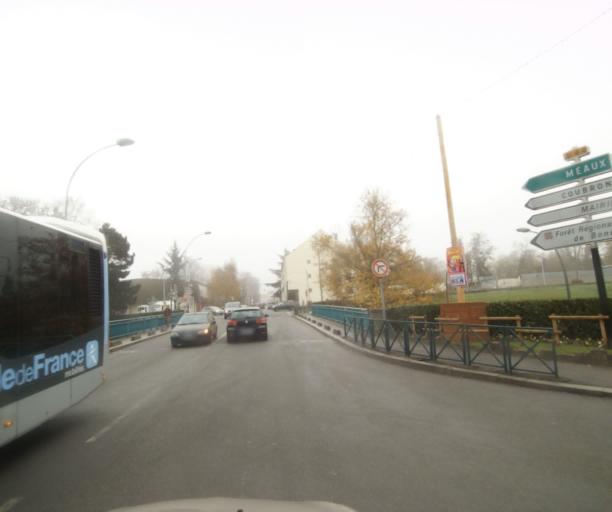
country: FR
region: Ile-de-France
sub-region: Departement de Seine-Saint-Denis
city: Vaujours
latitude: 48.9339
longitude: 2.5666
